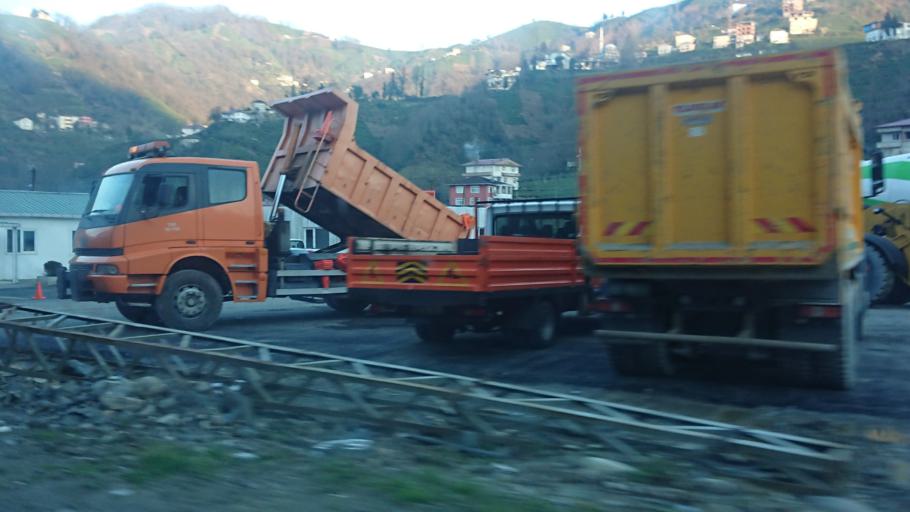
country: TR
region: Rize
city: Gundogdu
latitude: 41.0255
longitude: 40.5783
